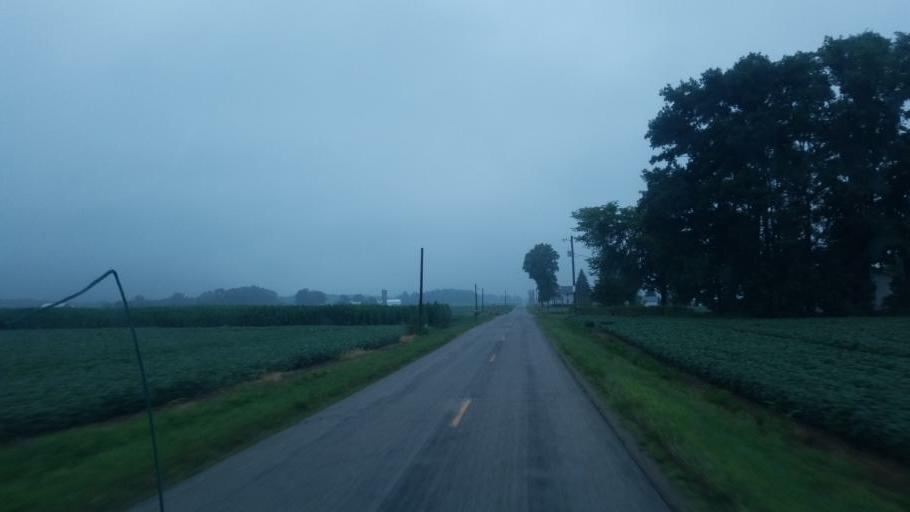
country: US
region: Ohio
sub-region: Defiance County
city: Hicksville
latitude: 41.3189
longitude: -84.7284
